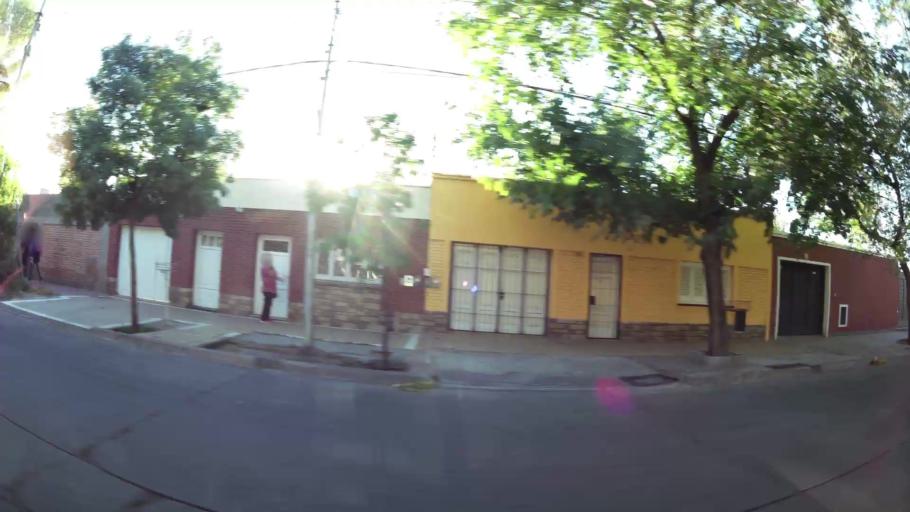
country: AR
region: Mendoza
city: Las Heras
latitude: -32.8649
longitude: -68.8382
